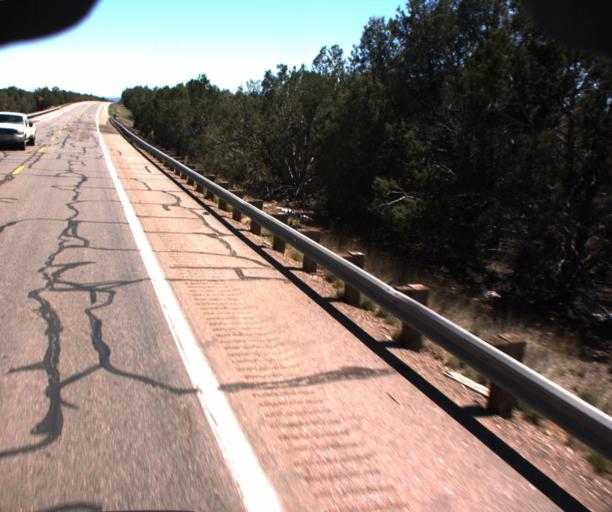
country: US
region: Arizona
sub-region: Yavapai County
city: Paulden
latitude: 35.0539
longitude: -112.3971
